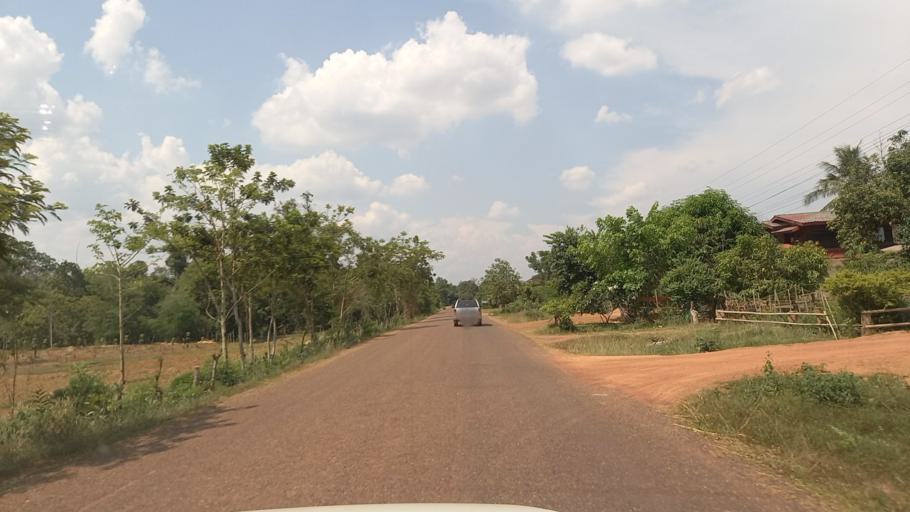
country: LA
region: Bolikhamxai
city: Muang Pakxan
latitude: 18.4241
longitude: 103.7073
